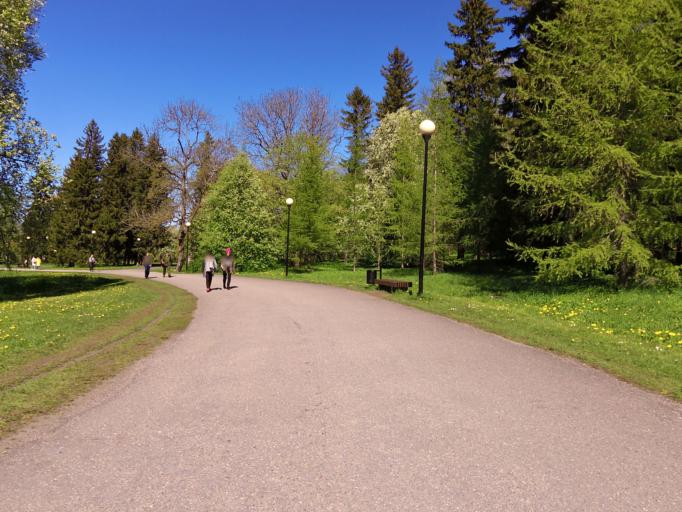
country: EE
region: Harju
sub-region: Tallinna linn
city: Tallinn
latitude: 59.4392
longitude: 24.8011
